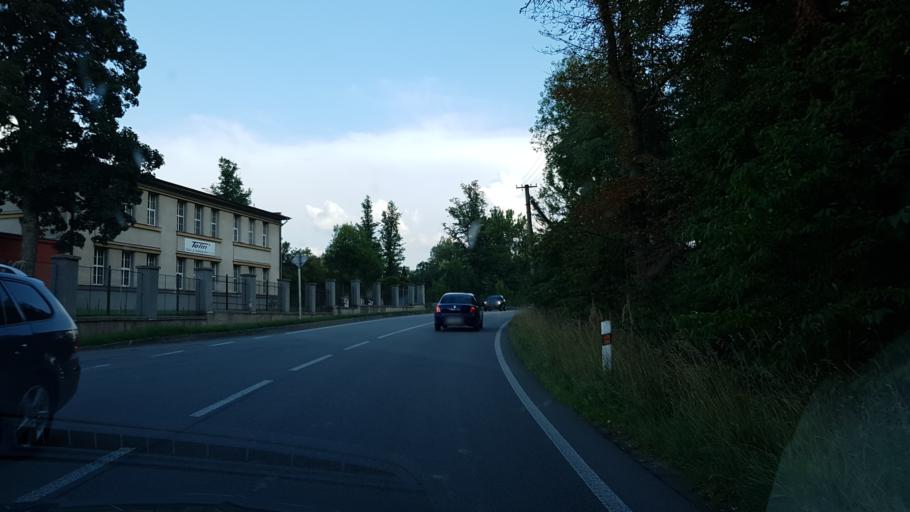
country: CZ
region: Pardubicky
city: Zamberk
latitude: 50.0926
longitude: 16.4526
